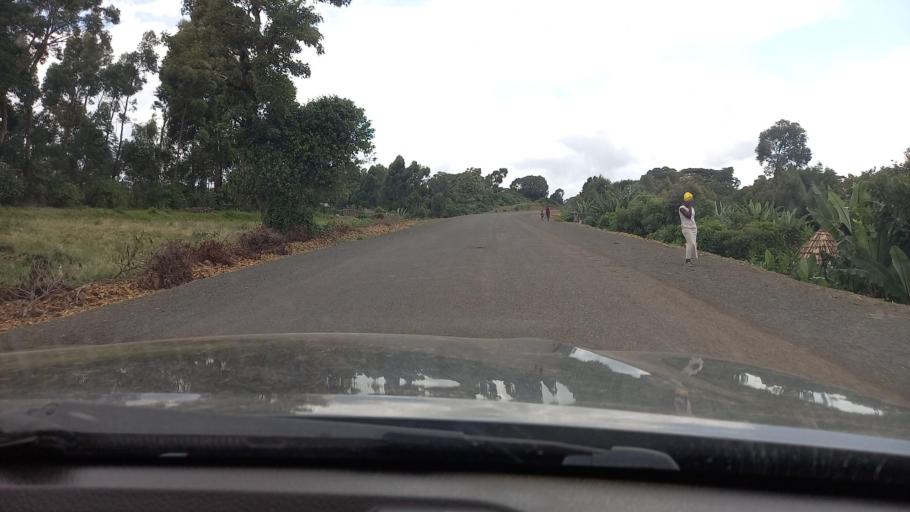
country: ET
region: Southern Nations, Nationalities, and People's Region
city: Mizan Teferi
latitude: 6.2099
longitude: 35.6131
